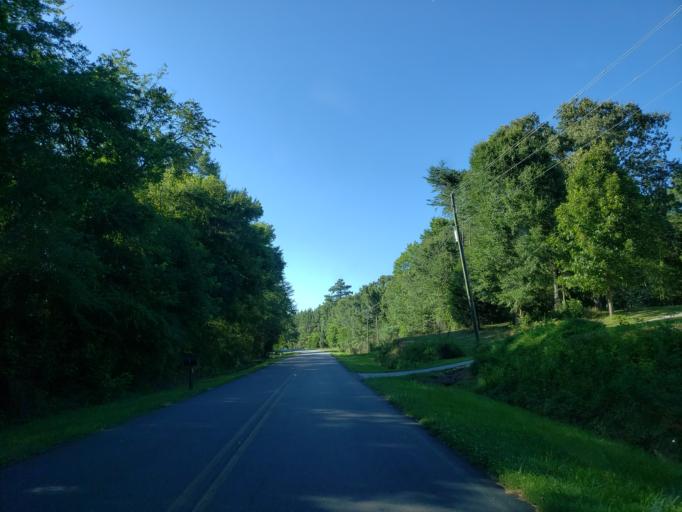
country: US
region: Georgia
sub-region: Bartow County
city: Euharlee
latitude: 34.1068
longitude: -85.0028
